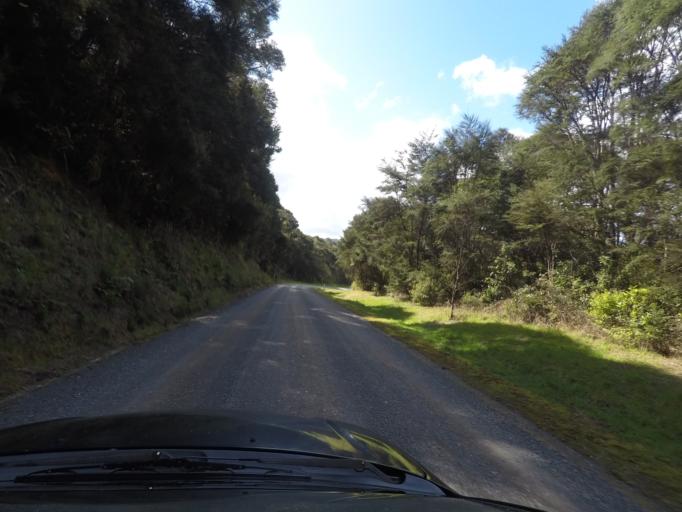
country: NZ
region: Auckland
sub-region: Auckland
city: Red Hill
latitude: -37.0949
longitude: 175.1514
